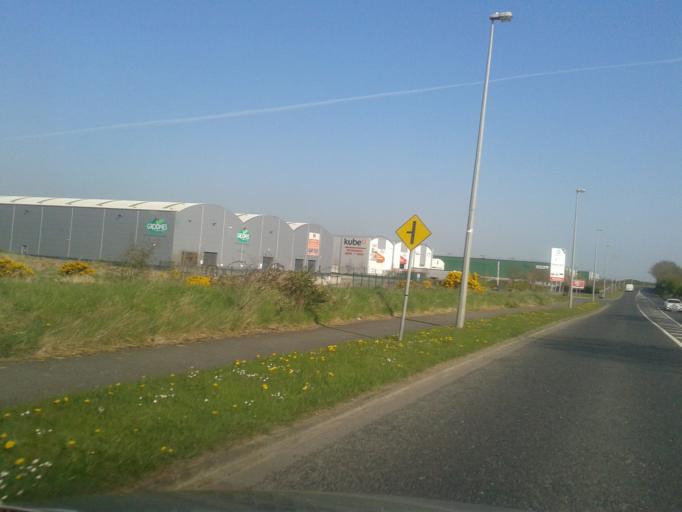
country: IE
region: Leinster
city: Balrothery
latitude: 53.5673
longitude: -6.2093
